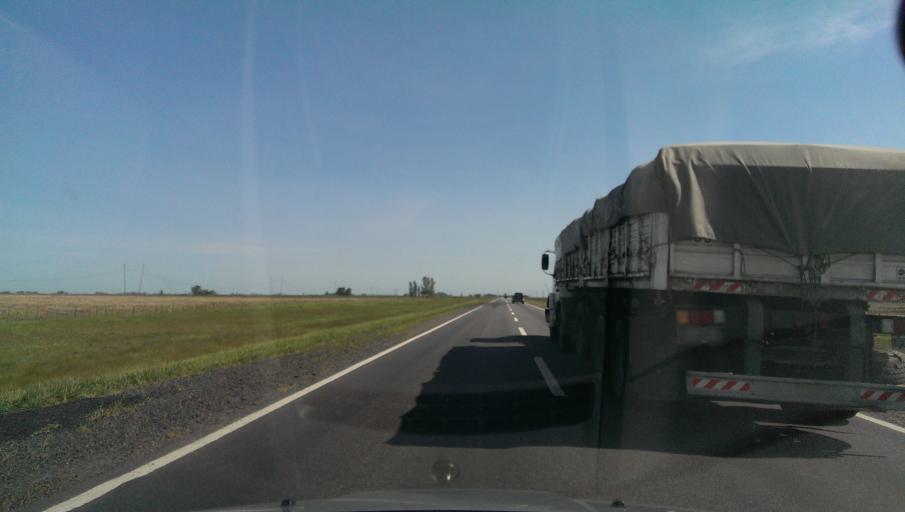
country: AR
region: Buenos Aires
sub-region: Partido de Azul
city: Azul
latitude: -36.6207
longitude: -59.6891
